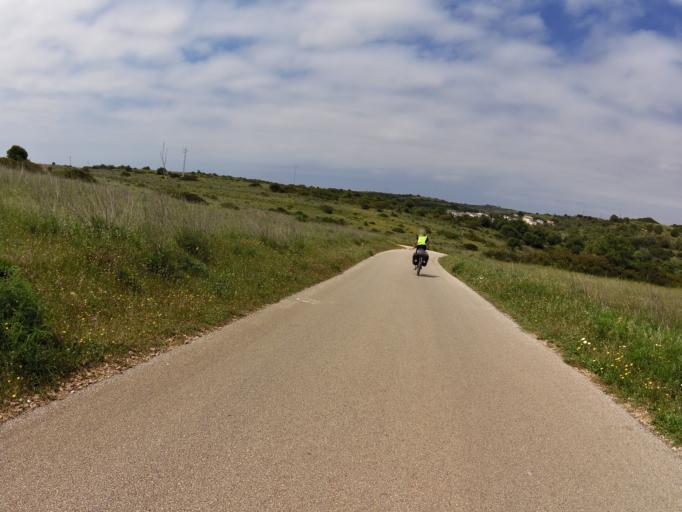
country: PT
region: Faro
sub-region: Vila do Bispo
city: Vila do Bispo
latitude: 37.0664
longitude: -8.8675
